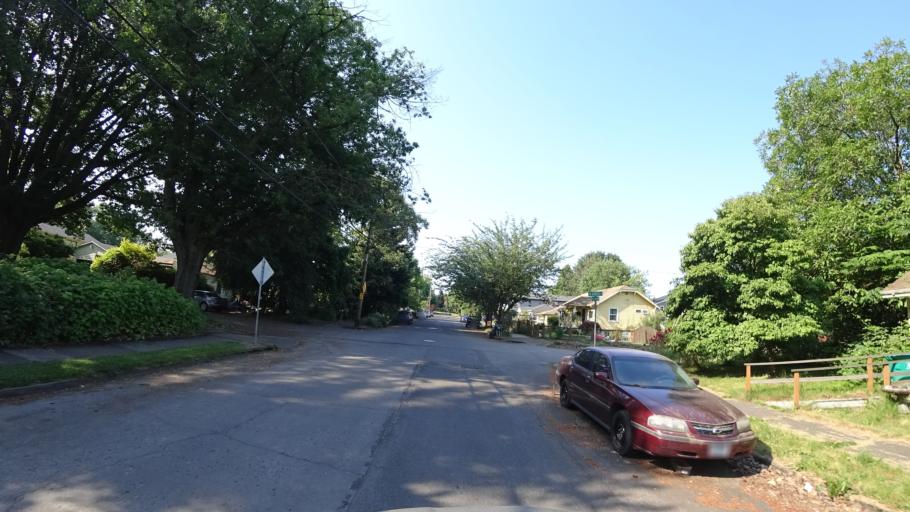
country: US
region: Oregon
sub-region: Washington County
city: West Haven
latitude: 45.5933
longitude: -122.7399
